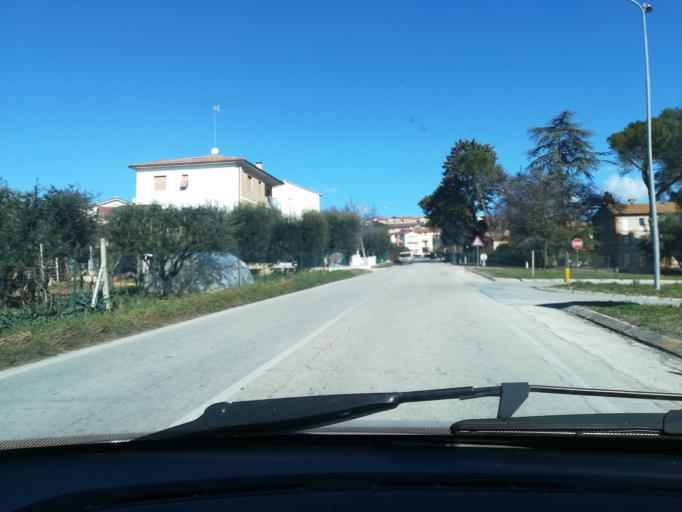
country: IT
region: The Marches
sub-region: Provincia di Macerata
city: Montecassiano
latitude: 43.3604
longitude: 13.4409
